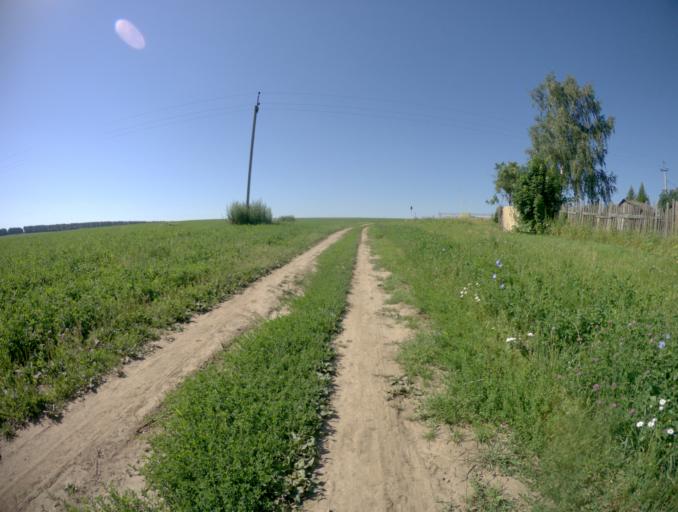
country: RU
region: Nizjnij Novgorod
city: Reshetikha
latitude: 56.1651
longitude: 43.3555
